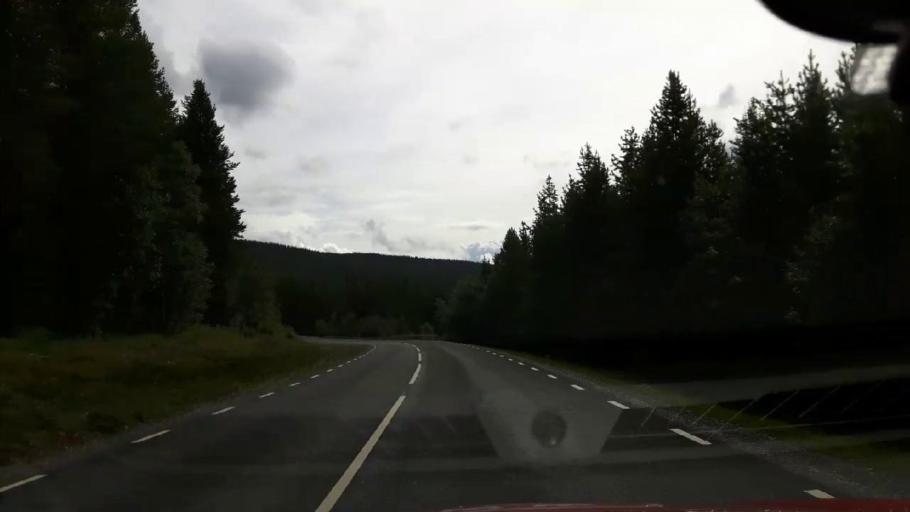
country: NO
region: Nord-Trondelag
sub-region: Lierne
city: Sandvika
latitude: 64.6372
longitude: 14.1379
